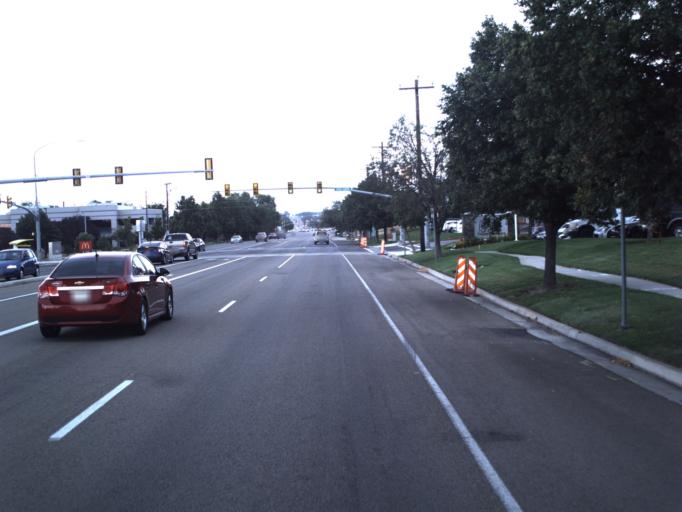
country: US
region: Utah
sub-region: Salt Lake County
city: White City
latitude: 40.5466
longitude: -111.8910
